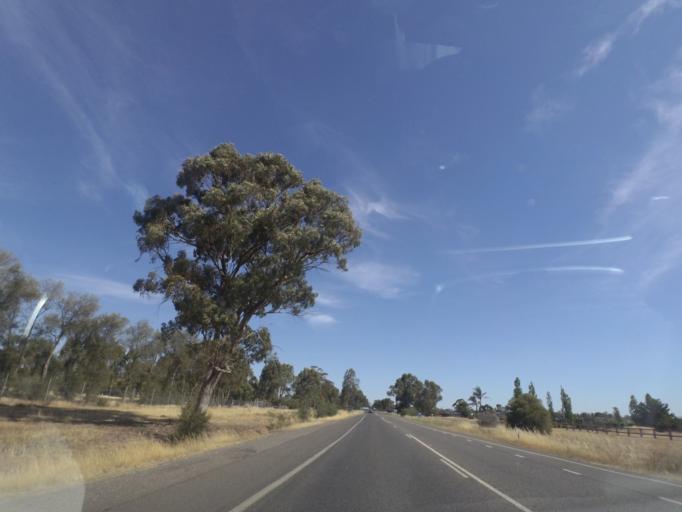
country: AU
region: Victoria
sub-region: Greater Shepparton
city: Shepparton
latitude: -36.4373
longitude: 145.3889
